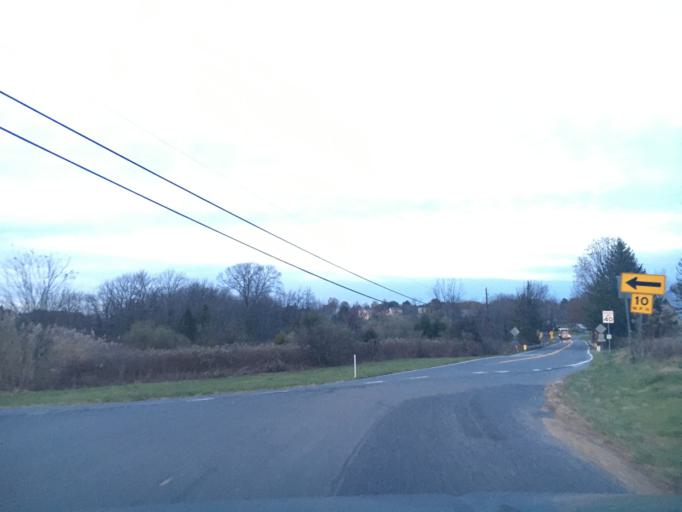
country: US
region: Pennsylvania
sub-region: Lehigh County
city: Schnecksville
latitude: 40.6962
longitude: -75.5829
